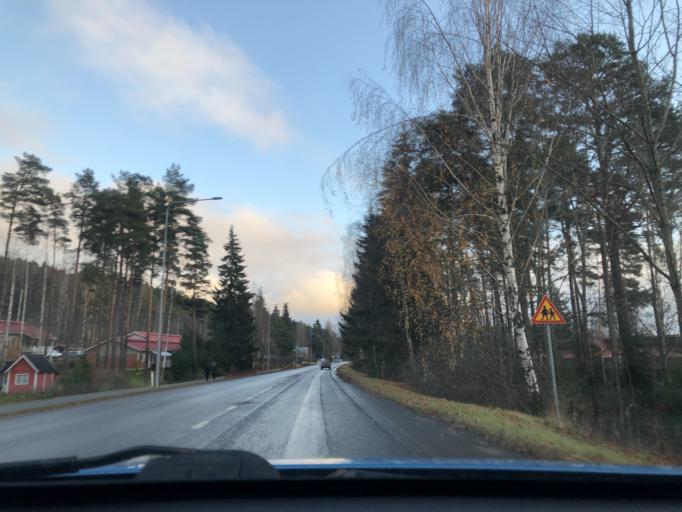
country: FI
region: Pirkanmaa
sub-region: Tampere
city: Kangasala
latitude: 61.4685
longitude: 24.0450
